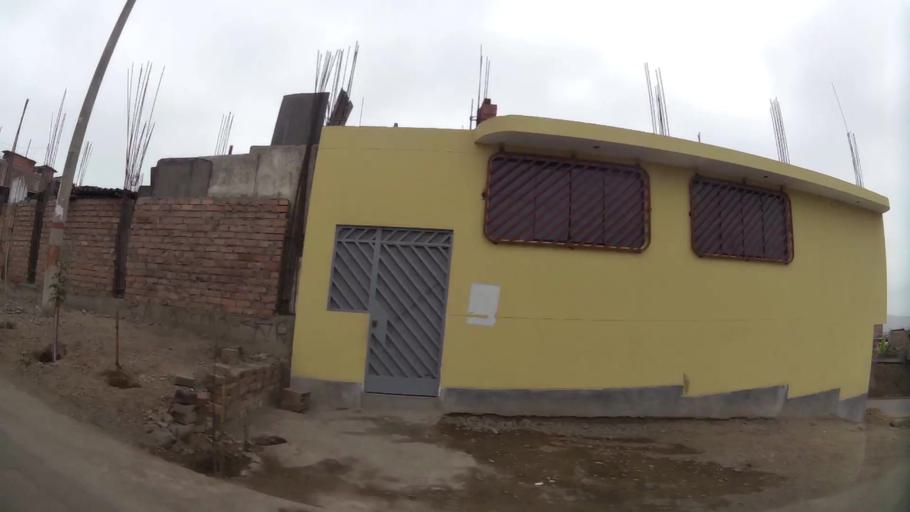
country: PE
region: Lima
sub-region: Lima
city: Surco
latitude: -12.1815
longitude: -76.9610
